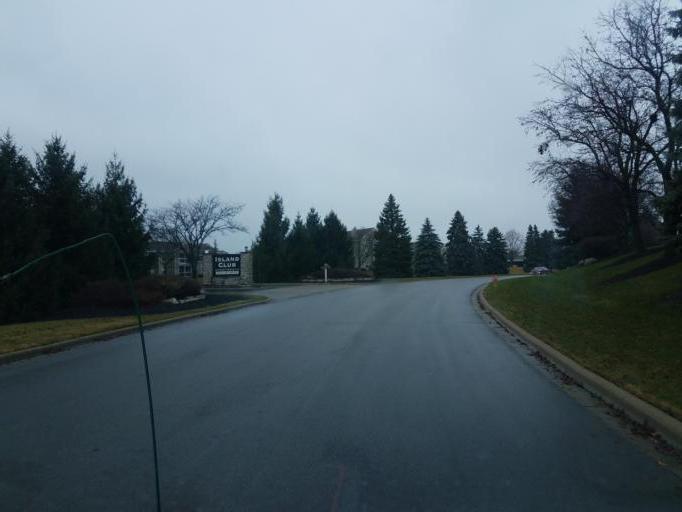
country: US
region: Ohio
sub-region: Franklin County
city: Dublin
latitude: 40.0671
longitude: -83.0757
